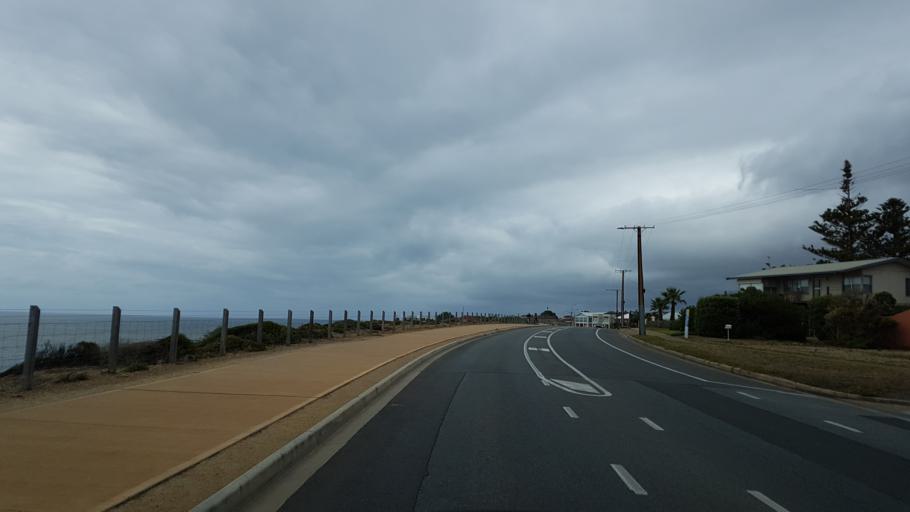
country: AU
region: South Australia
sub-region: Onkaparinga
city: Port Willunga
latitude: -35.2833
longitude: 138.4434
